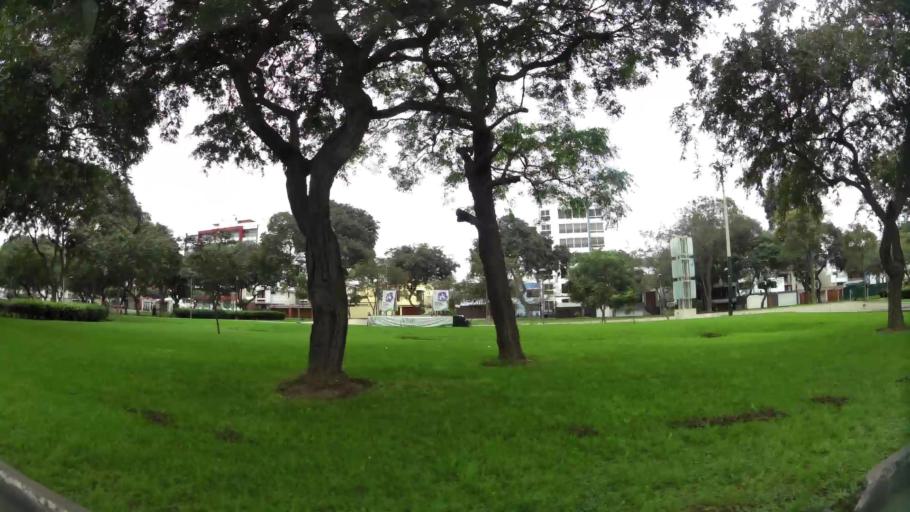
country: PE
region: Lima
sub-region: Lima
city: San Luis
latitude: -12.0943
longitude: -77.0192
